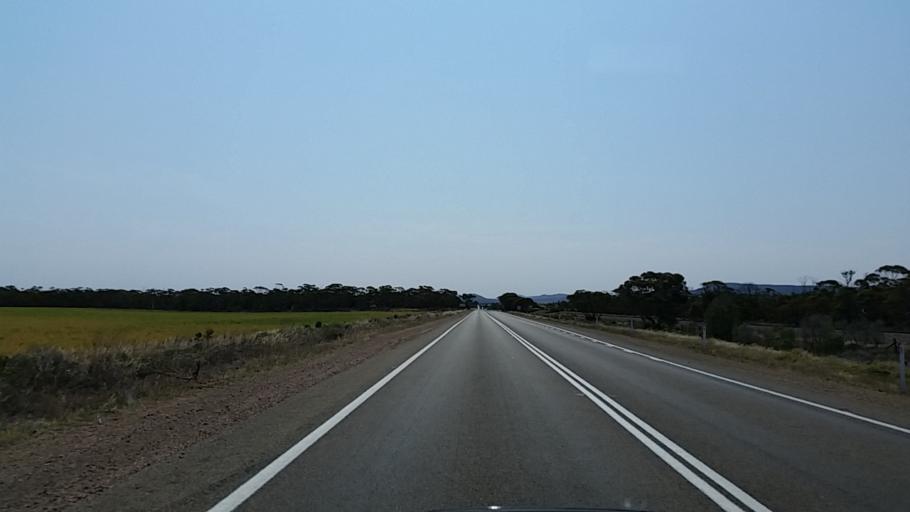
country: AU
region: South Australia
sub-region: Port Pirie City and Dists
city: Port Pirie
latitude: -32.9165
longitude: 137.9824
